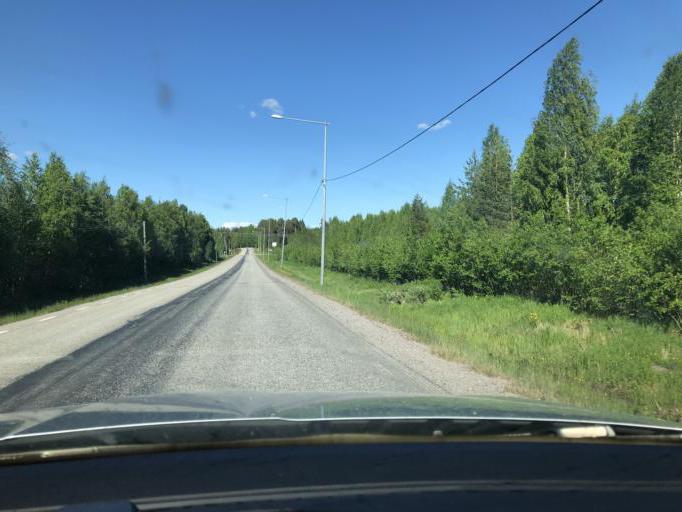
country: SE
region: Norrbotten
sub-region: Kalix Kommun
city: Kalix
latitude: 65.8705
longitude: 23.1483
